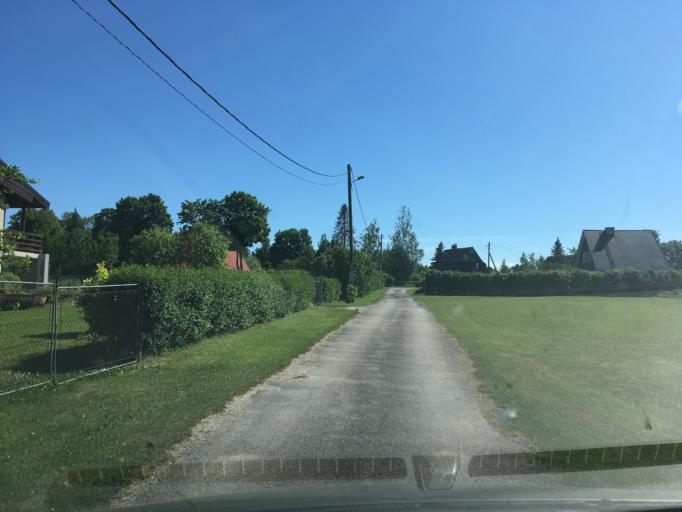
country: EE
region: Harju
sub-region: Raasiku vald
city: Raasiku
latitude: 59.1843
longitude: 25.1797
